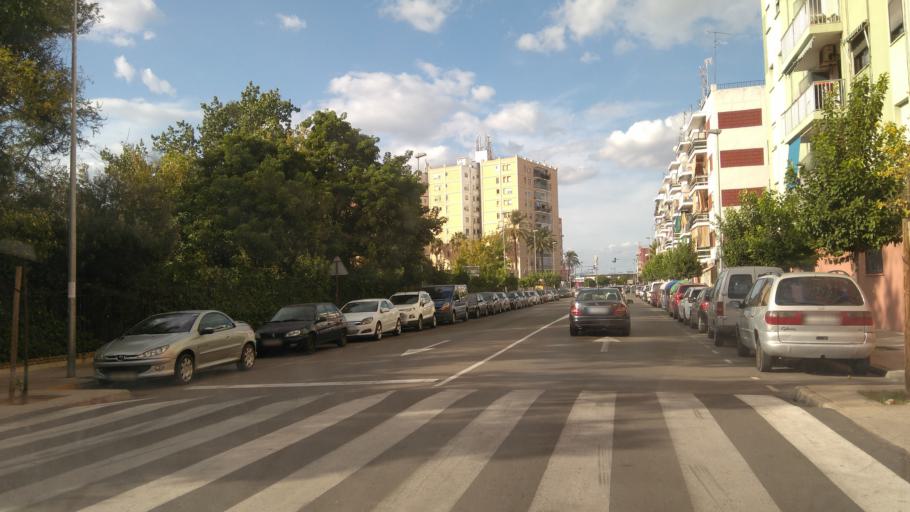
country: ES
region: Valencia
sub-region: Provincia de Valencia
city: Alzira
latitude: 39.1571
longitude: -0.4284
